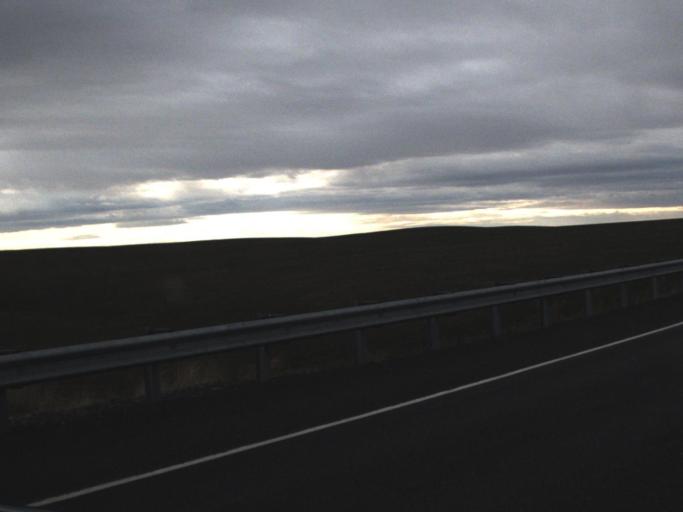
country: US
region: Washington
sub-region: Adams County
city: Ritzville
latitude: 46.7953
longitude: -118.4029
